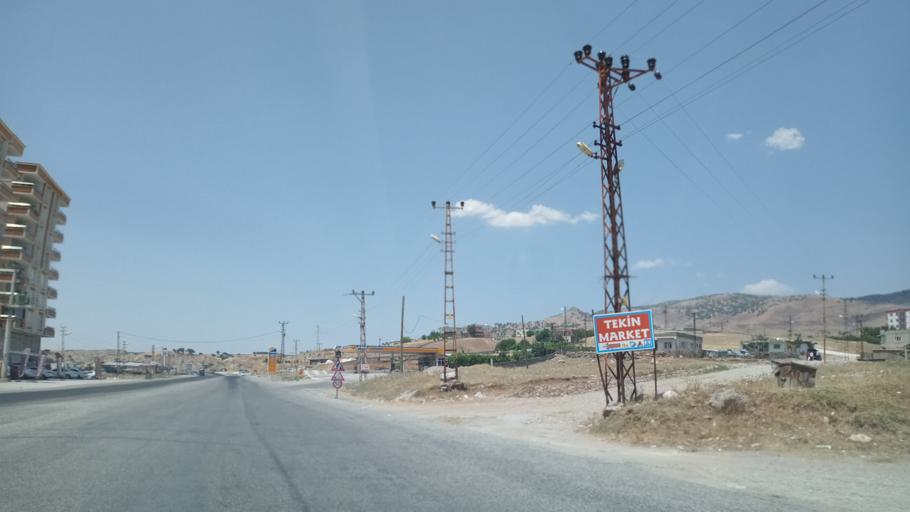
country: TR
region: Batman
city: Kozluk
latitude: 38.1681
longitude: 41.4893
